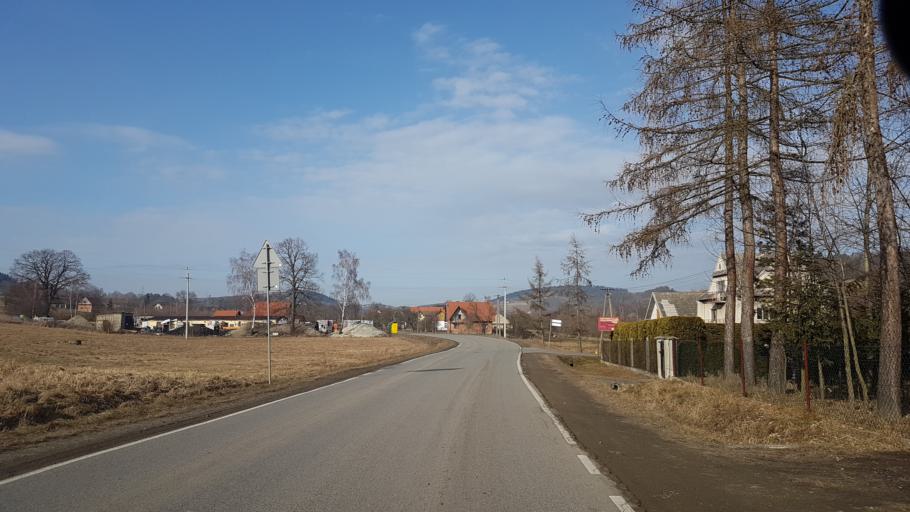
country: PL
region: Lesser Poland Voivodeship
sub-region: Powiat limanowski
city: Lukowica
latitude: 49.6499
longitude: 20.5010
